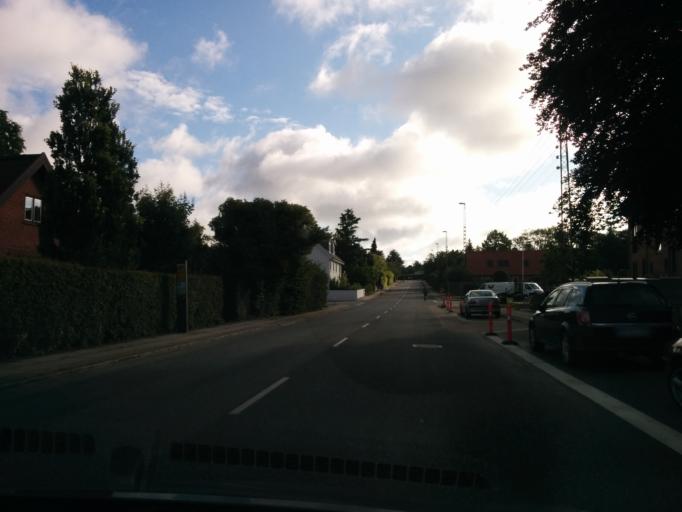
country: DK
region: Central Jutland
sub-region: Arhus Kommune
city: Arhus
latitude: 56.1220
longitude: 10.1897
